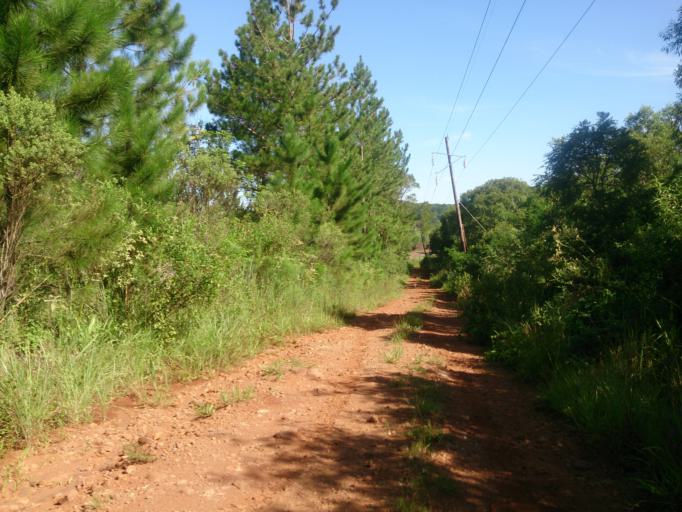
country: AR
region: Misiones
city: Campo Viera
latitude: -27.3635
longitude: -55.0493
